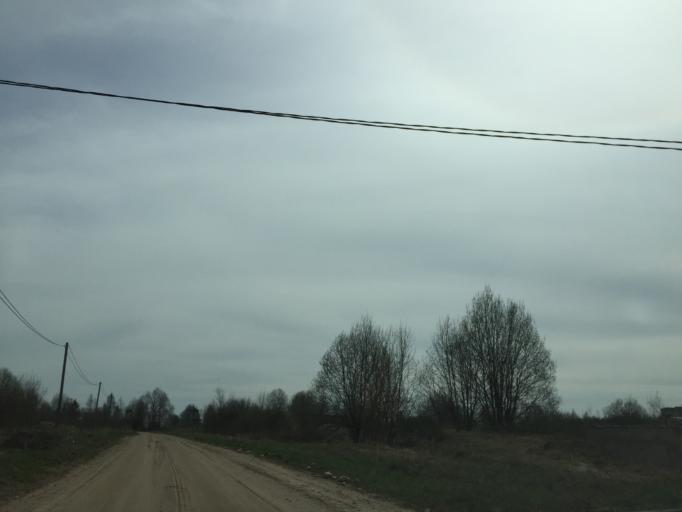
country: LV
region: Ludzas Rajons
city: Ludza
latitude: 56.5151
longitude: 27.5413
